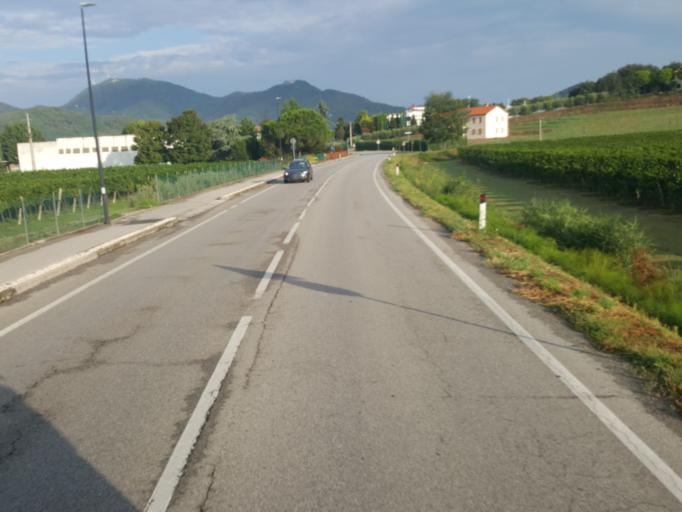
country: IT
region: Veneto
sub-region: Provincia di Padova
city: Battaglia Terme
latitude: 45.2983
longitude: 11.7590
